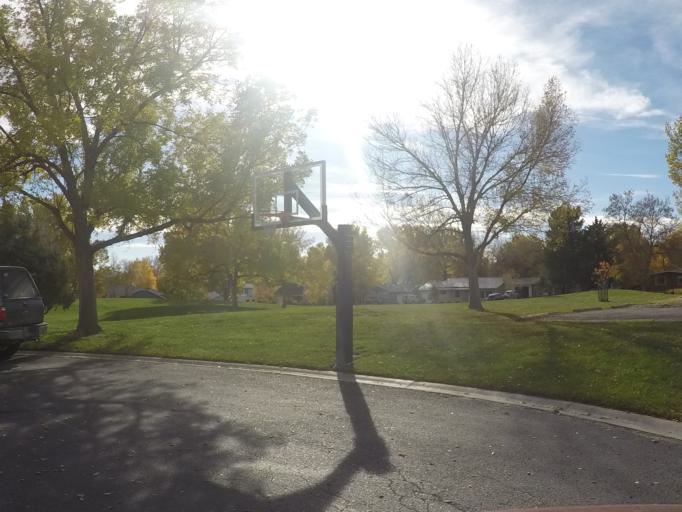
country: US
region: Montana
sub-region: Yellowstone County
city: Billings
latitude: 45.7981
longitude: -108.5607
